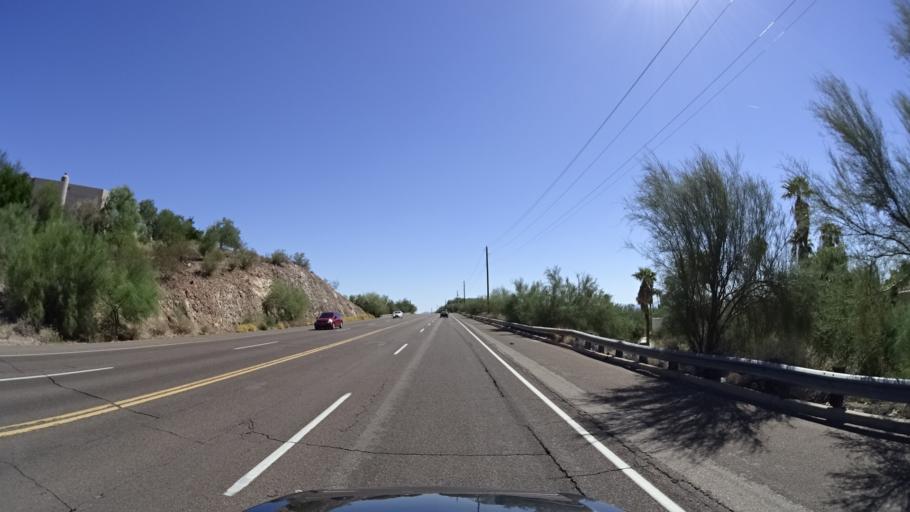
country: US
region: Arizona
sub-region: Maricopa County
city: Paradise Valley
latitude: 33.5245
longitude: -112.0132
